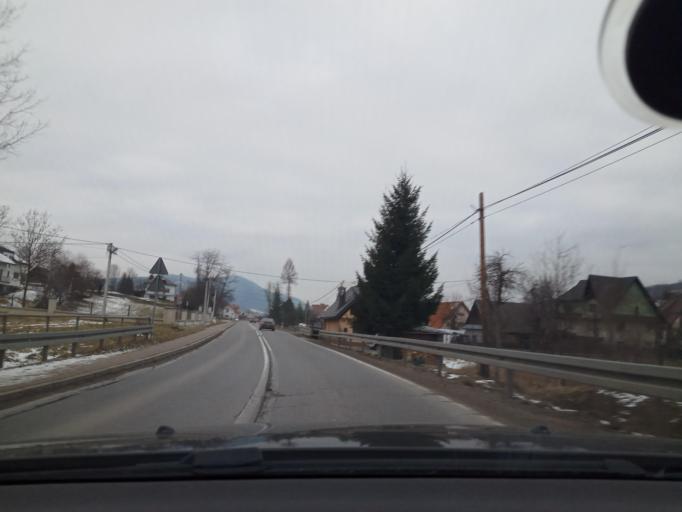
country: PL
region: Lesser Poland Voivodeship
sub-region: Powiat limanowski
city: Mszana Gorna
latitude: 49.6571
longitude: 20.1073
